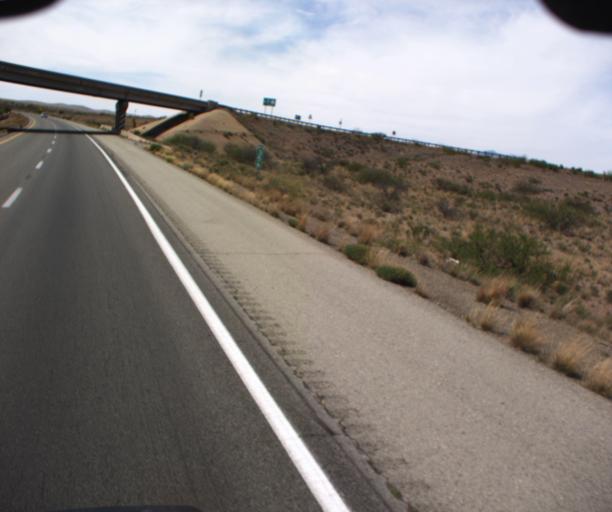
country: US
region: Arizona
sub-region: Cochise County
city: Willcox
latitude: 32.3621
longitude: -109.6200
